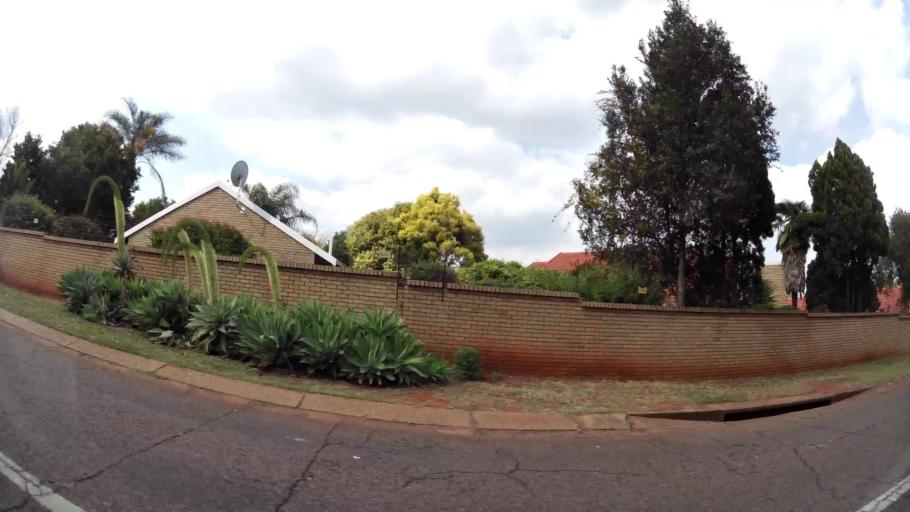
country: ZA
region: Gauteng
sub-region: City of Tshwane Metropolitan Municipality
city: Pretoria
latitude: -25.7506
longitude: 28.3140
